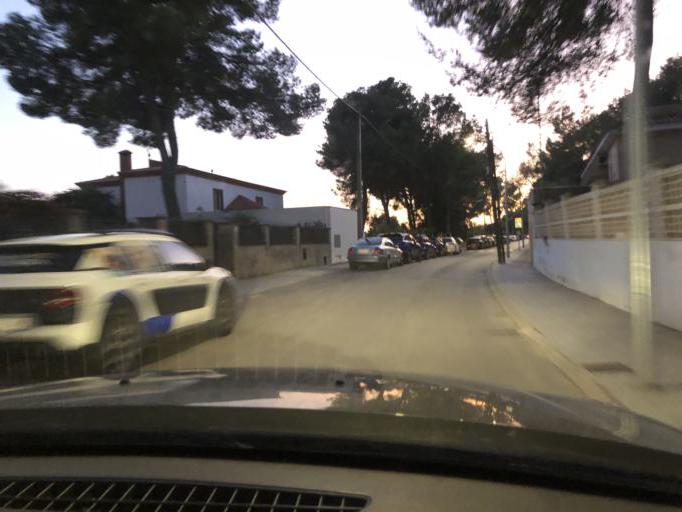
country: ES
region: Balearic Islands
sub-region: Illes Balears
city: Santa Ponsa
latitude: 39.5220
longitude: 2.4887
